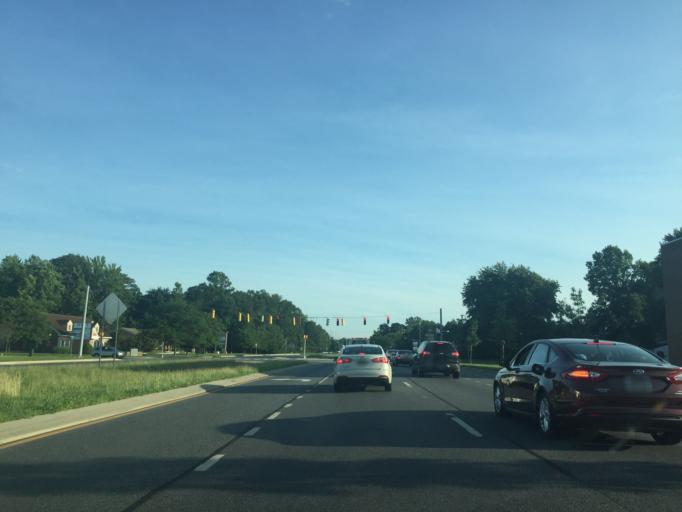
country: US
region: Delaware
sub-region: Kent County
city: Dover
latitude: 39.1531
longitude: -75.5138
